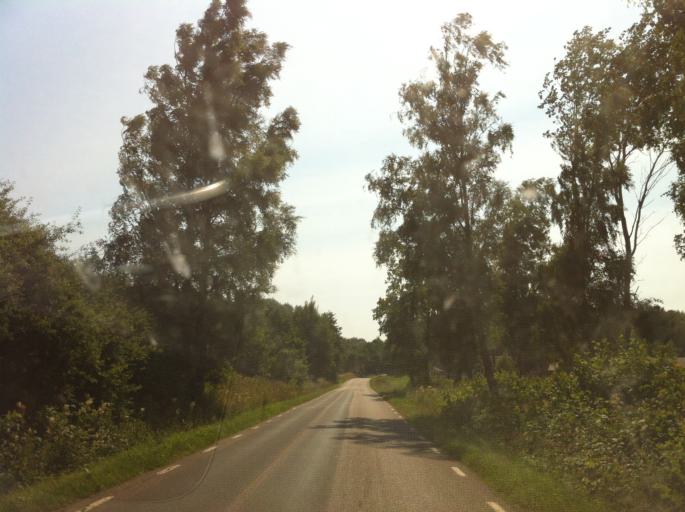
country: SE
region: Skane
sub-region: Hoors Kommun
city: Hoeoer
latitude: 56.0056
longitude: 13.4900
